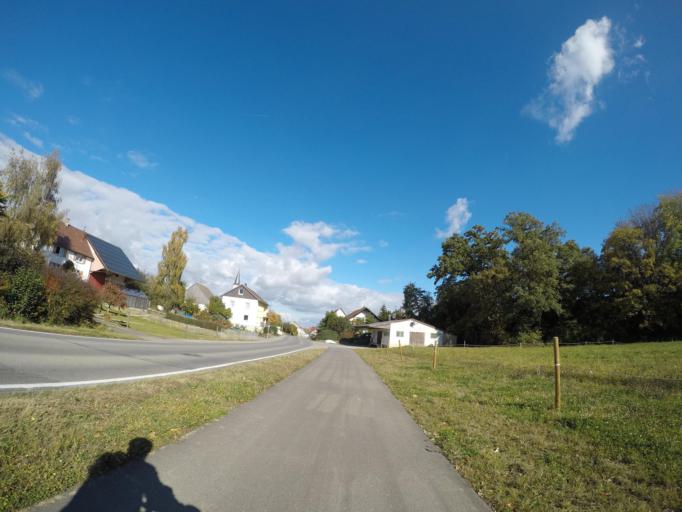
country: DE
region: Baden-Wuerttemberg
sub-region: Tuebingen Region
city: Grundsheim
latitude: 48.1457
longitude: 9.6644
